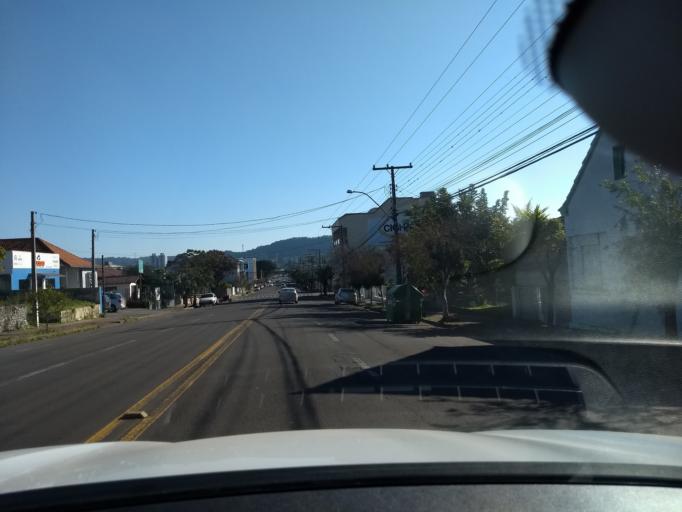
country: BR
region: Rio Grande do Sul
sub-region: Santa Cruz Do Sul
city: Santa Cruz do Sul
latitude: -29.7141
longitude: -52.4357
